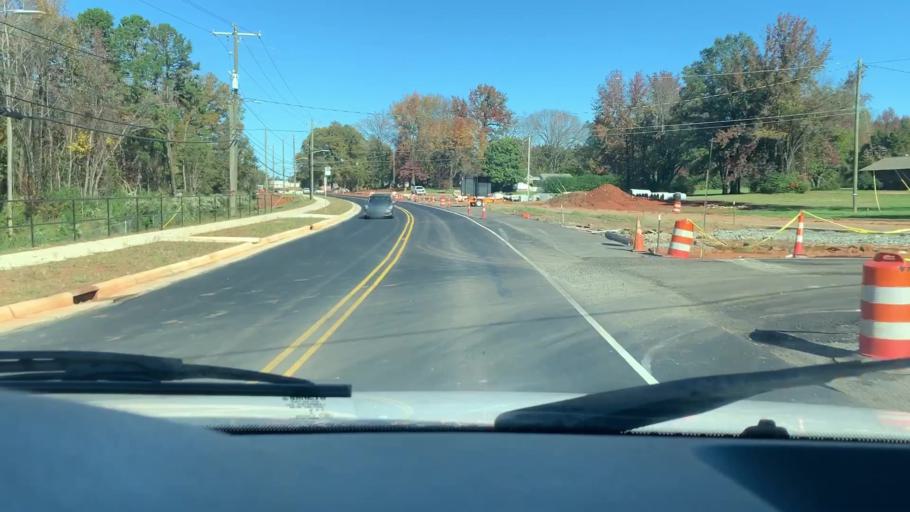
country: US
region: North Carolina
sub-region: Mecklenburg County
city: Charlotte
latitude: 35.3008
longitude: -80.8557
